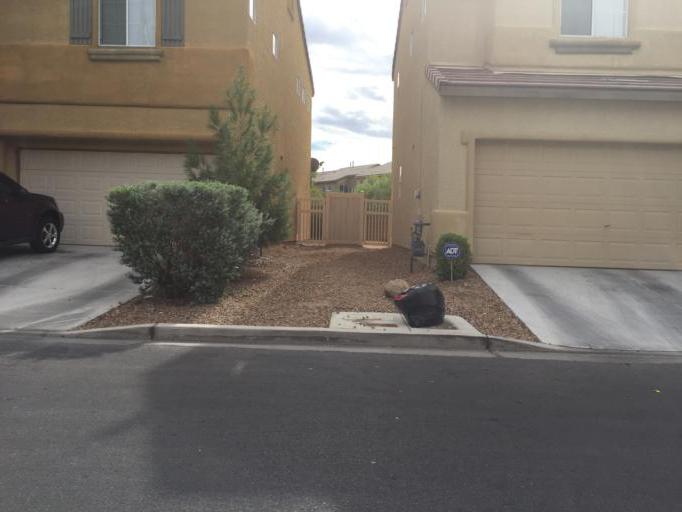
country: US
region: Nevada
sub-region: Clark County
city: Whitney
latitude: 36.1163
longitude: -115.0344
